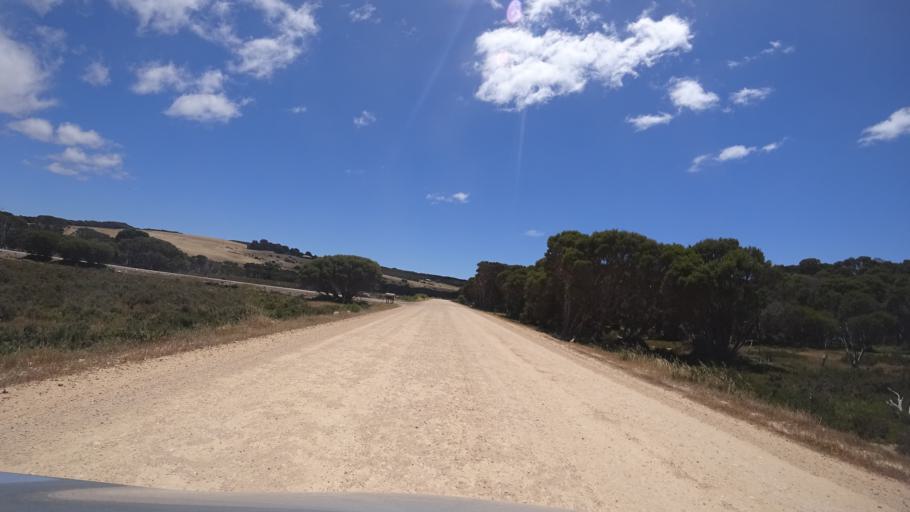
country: AU
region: South Australia
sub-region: Yankalilla
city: Normanville
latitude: -35.8000
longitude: 138.0651
